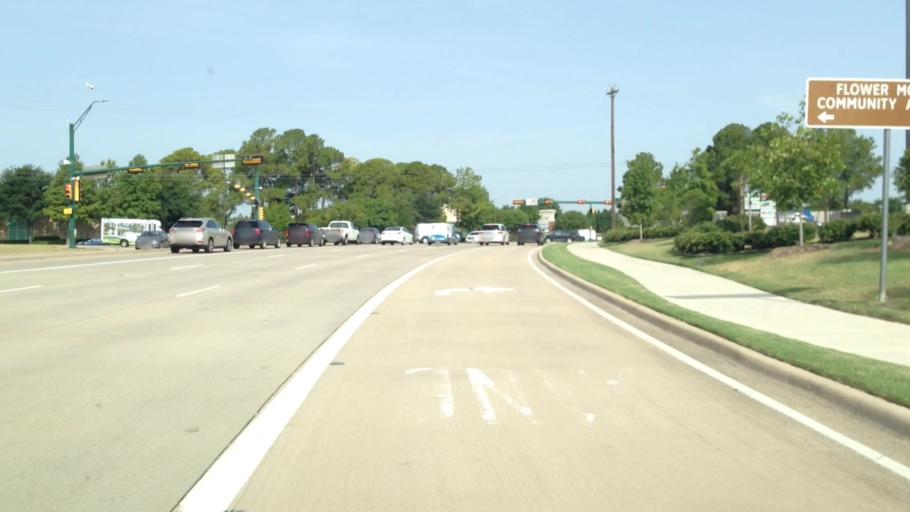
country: US
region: Texas
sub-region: Denton County
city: Flower Mound
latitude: 33.0103
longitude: -97.0439
